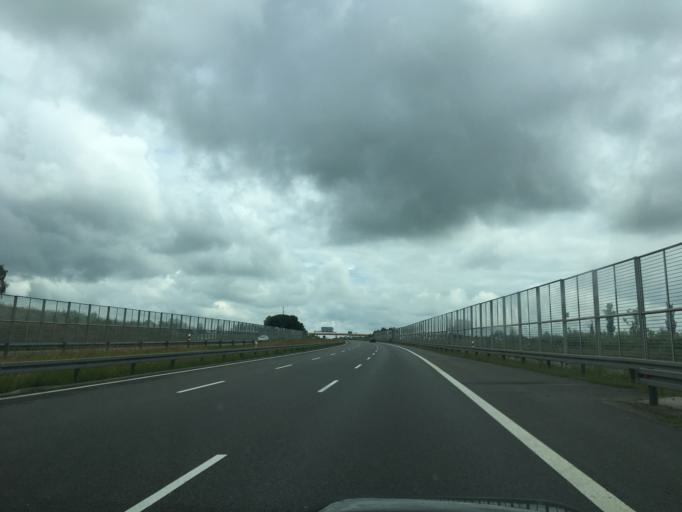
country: PL
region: Lublin Voivodeship
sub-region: Powiat lubelski
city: Lublin
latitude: 51.2978
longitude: 22.5293
